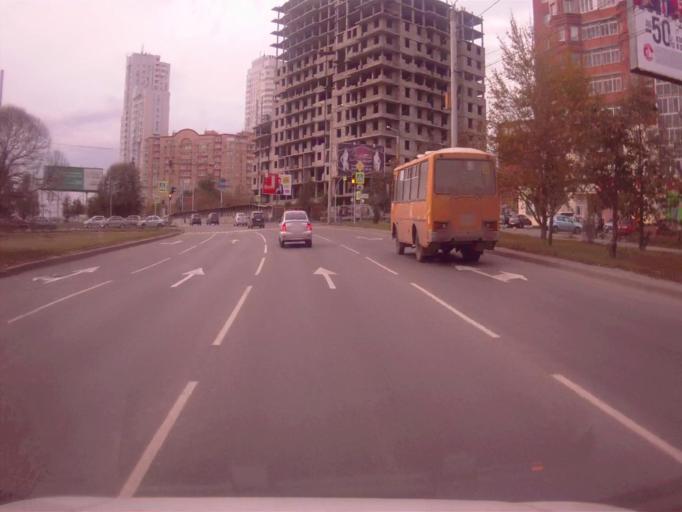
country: RU
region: Chelyabinsk
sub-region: Gorod Chelyabinsk
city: Chelyabinsk
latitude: 55.1740
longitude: 61.3960
